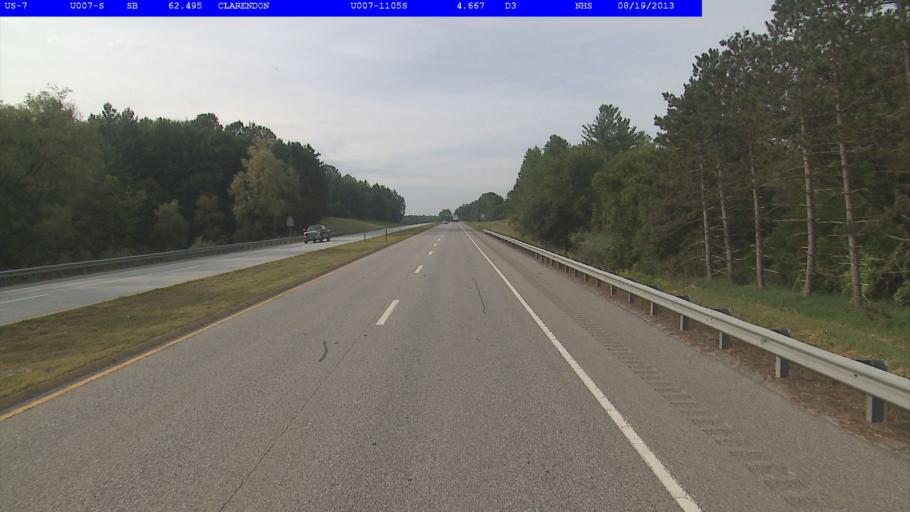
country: US
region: Vermont
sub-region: Rutland County
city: Rutland
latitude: 43.5589
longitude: -72.9646
